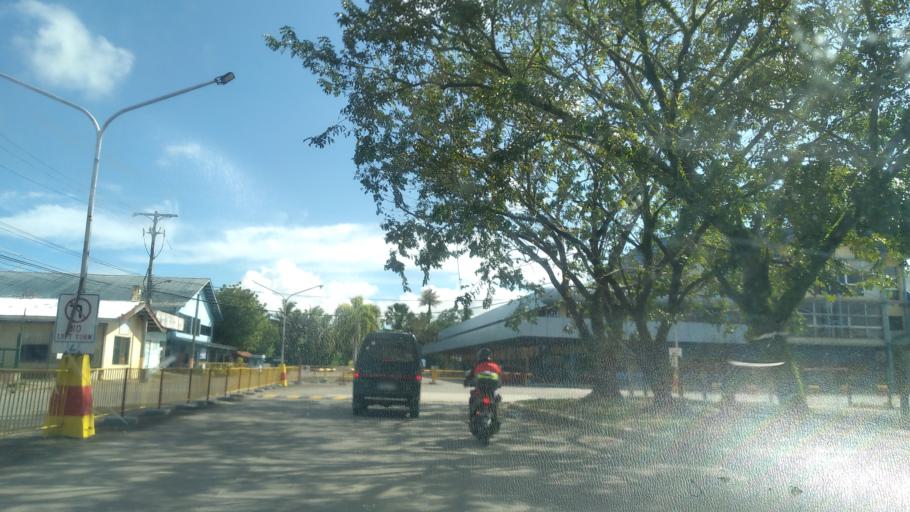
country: PH
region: Calabarzon
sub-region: Province of Quezon
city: Lucena
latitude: 13.9591
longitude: 121.6173
